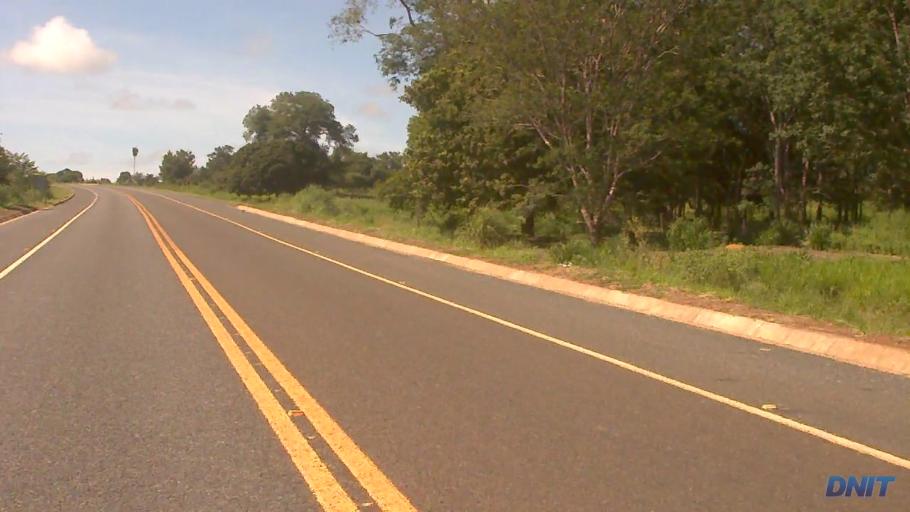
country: BR
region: Goias
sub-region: Sao Miguel Do Araguaia
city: Sao Miguel do Araguaia
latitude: -13.2936
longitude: -50.1771
